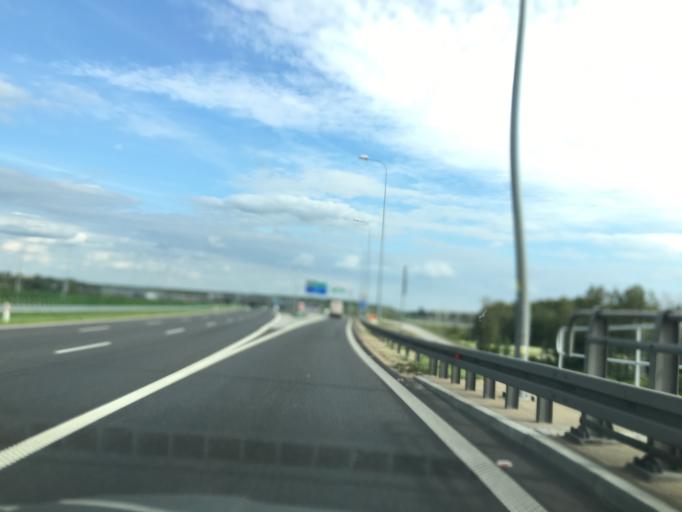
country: PL
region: Silesian Voivodeship
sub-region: Gliwice
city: Gliwice
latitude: 50.2837
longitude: 18.7181
